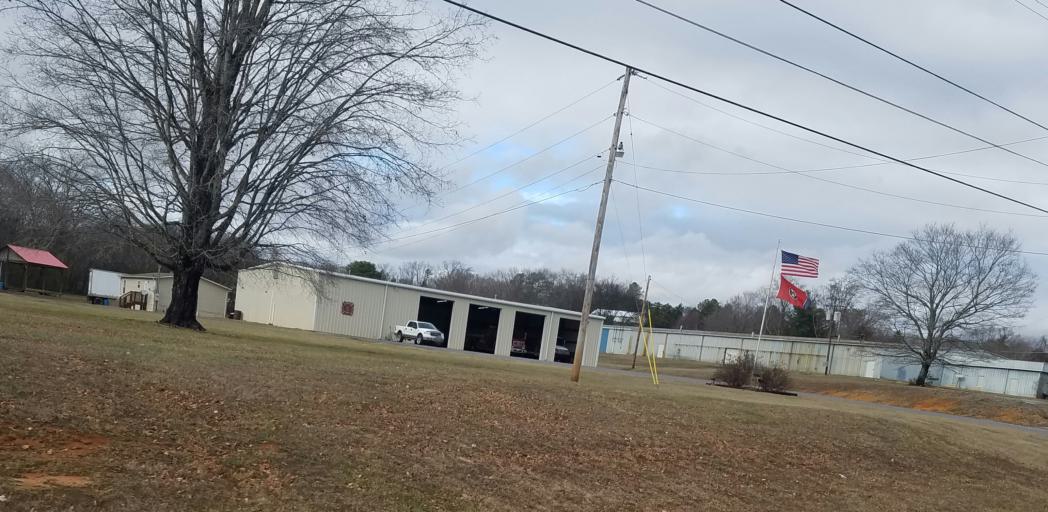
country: US
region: Tennessee
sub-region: McMinn County
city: Athens
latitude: 35.3738
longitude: -84.6992
